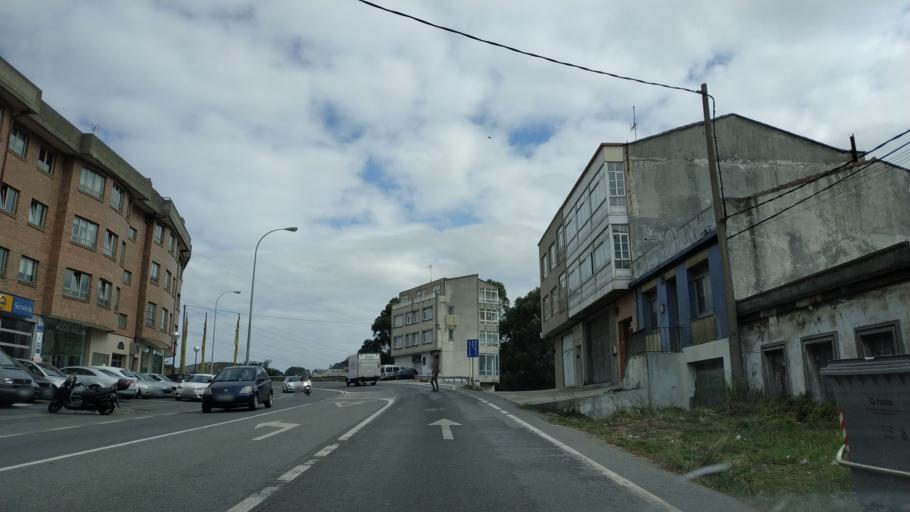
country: ES
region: Galicia
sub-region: Provincia da Coruna
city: Arteixo
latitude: 43.3250
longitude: -8.4737
